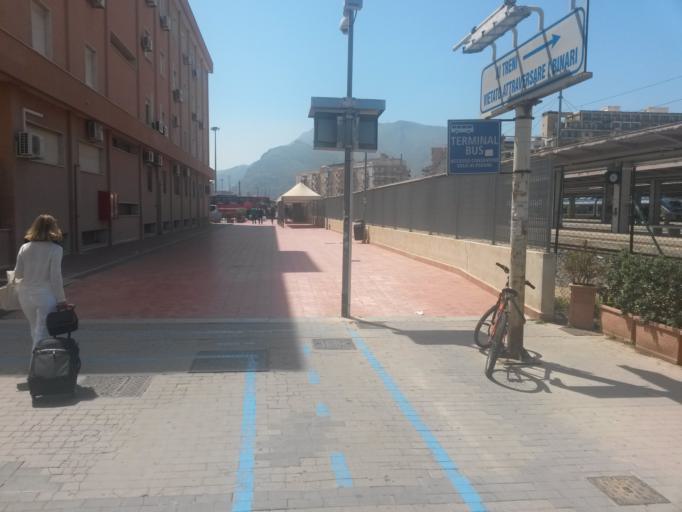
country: IT
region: Sicily
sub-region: Palermo
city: Palermo
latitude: 38.1087
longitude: 13.3686
